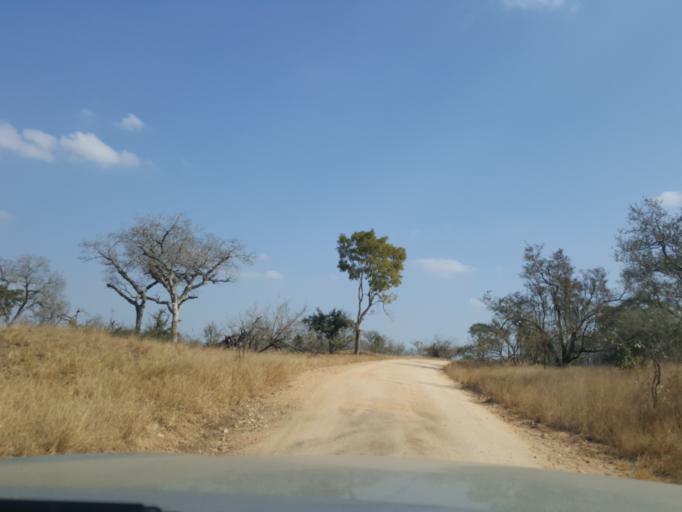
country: ZA
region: Mpumalanga
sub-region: Ehlanzeni District
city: Komatipoort
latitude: -25.2732
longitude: 31.7797
